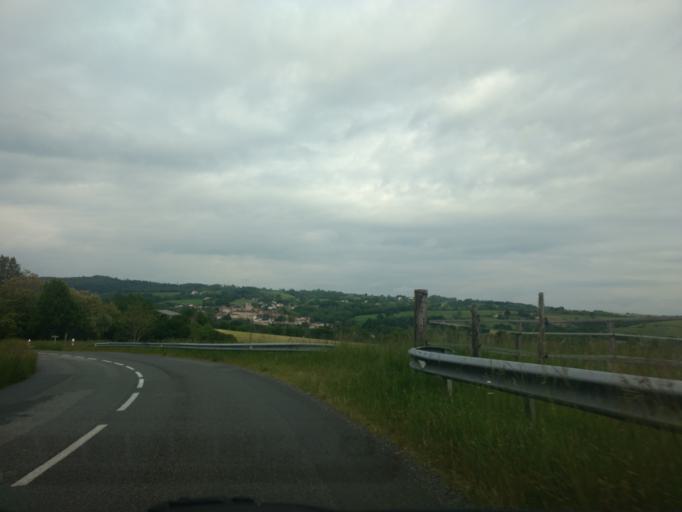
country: FR
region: Midi-Pyrenees
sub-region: Departement de l'Aveyron
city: Capdenac-Gare
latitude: 44.5444
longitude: 2.1322
